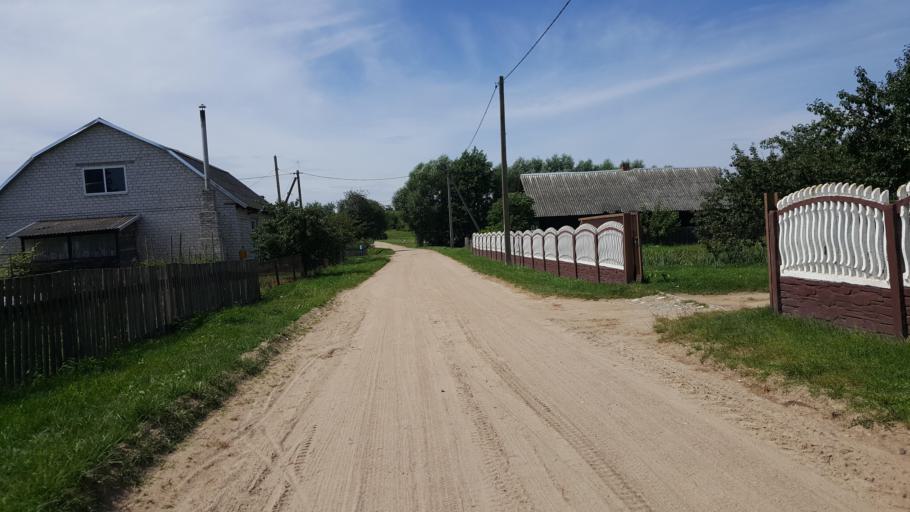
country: BY
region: Brest
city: Pruzhany
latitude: 52.5502
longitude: 24.2242
